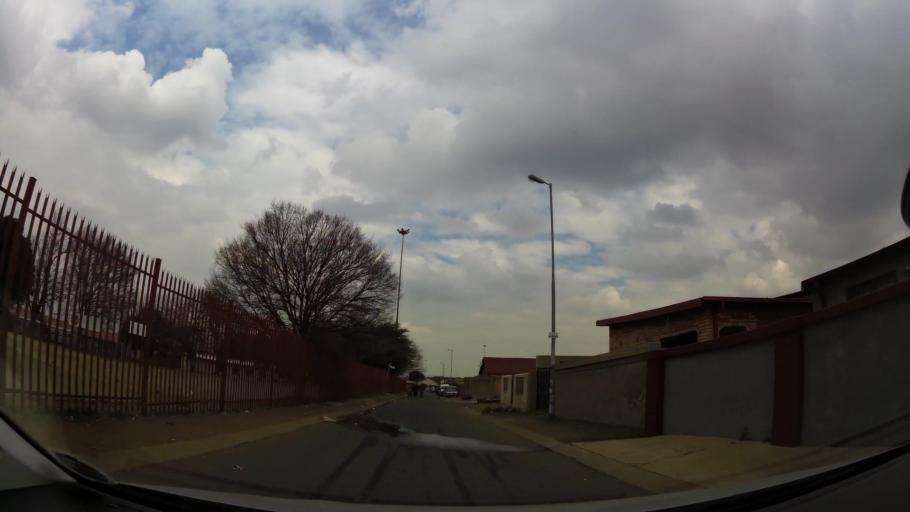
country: ZA
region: Gauteng
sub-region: City of Johannesburg Metropolitan Municipality
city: Soweto
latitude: -26.2603
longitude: 27.8612
